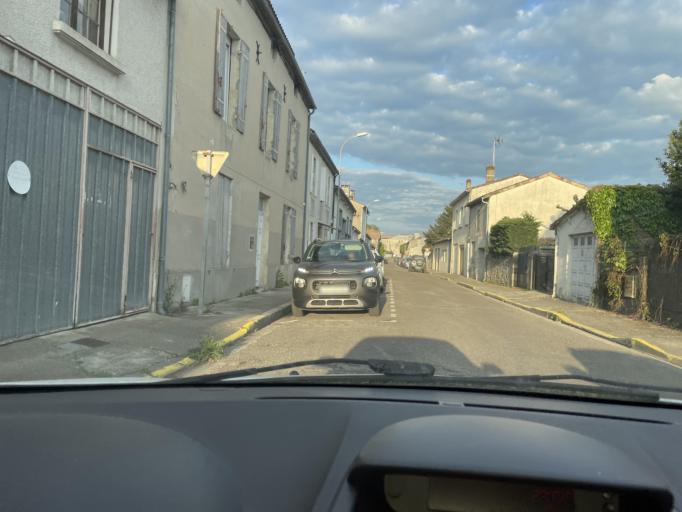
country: FR
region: Aquitaine
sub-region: Departement du Lot-et-Garonne
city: Casteljaloux
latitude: 44.3159
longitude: 0.0835
